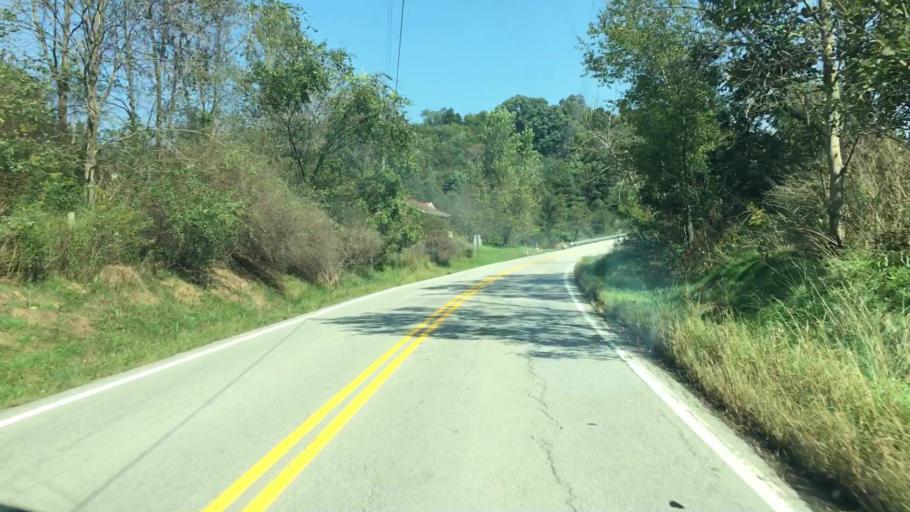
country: US
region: Pennsylvania
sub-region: Greene County
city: Waynesburg
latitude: 39.9995
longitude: -80.3533
